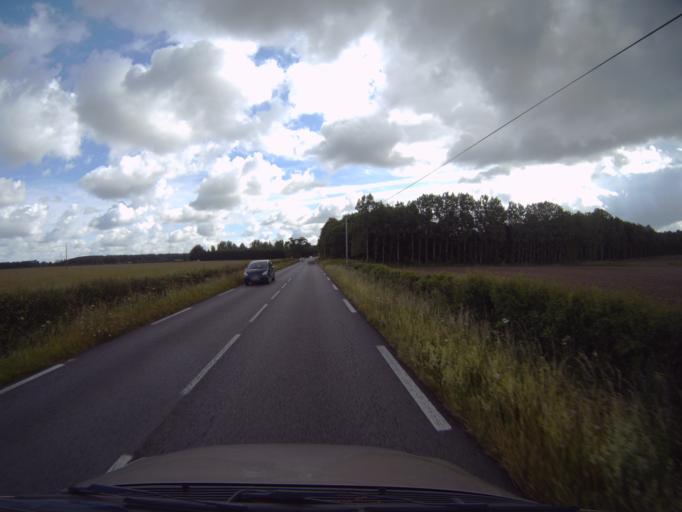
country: FR
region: Pays de la Loire
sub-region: Departement de la Vendee
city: Rocheserviere
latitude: 46.9181
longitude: -1.5411
